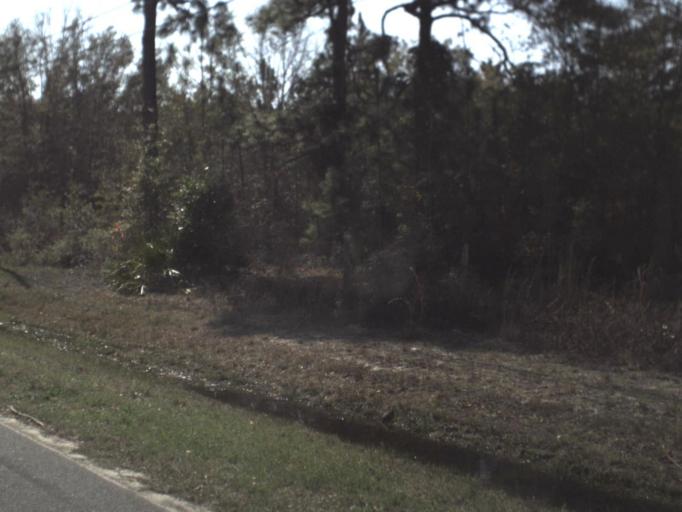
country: US
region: Florida
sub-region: Bay County
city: Pretty Bayou
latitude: 30.2108
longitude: -85.6718
